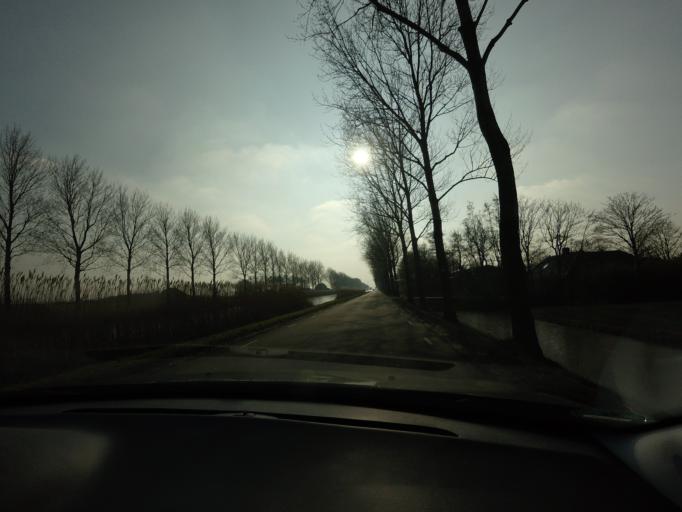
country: NL
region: North Holland
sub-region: Gemeente Alkmaar
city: Alkmaar
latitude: 52.5995
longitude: 4.7875
